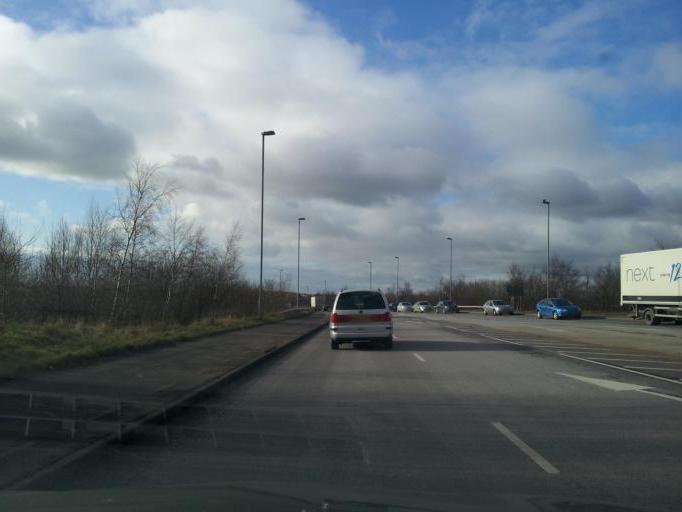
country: GB
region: England
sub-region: Nottinghamshire
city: Mansfield
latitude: 53.1270
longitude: -1.2265
